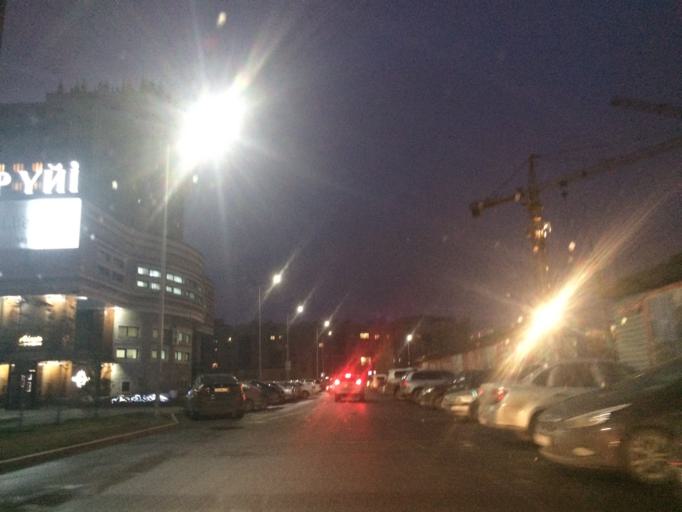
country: KZ
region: Astana Qalasy
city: Astana
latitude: 51.1405
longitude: 71.4163
